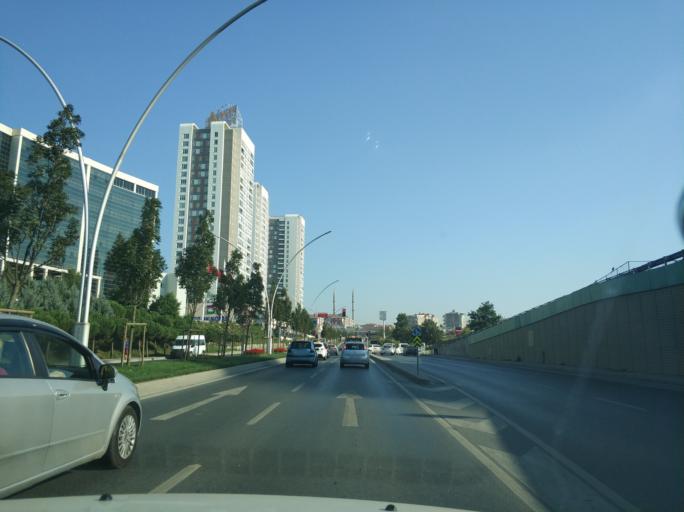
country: TR
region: Istanbul
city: Sultangazi
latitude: 41.0899
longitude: 28.9068
